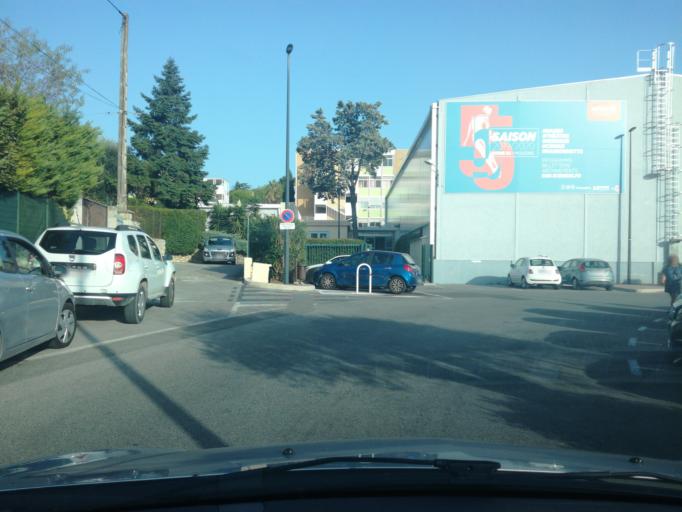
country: FR
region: Provence-Alpes-Cote d'Azur
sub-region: Departement des Alpes-Maritimes
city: Mougins
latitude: 43.5807
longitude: 6.9989
